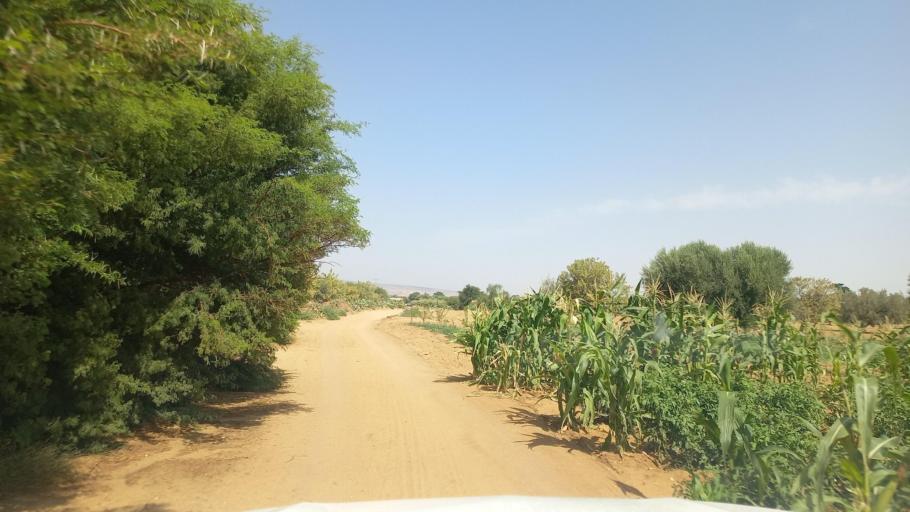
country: TN
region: Al Qasrayn
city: Kasserine
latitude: 35.2523
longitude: 9.0469
